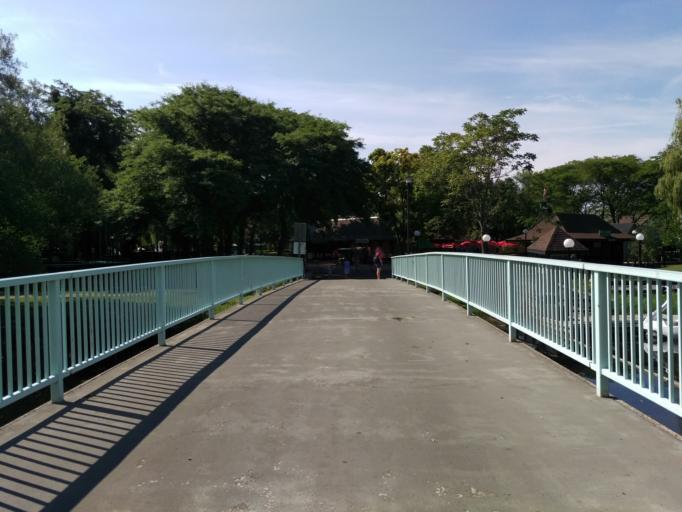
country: CA
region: Ontario
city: Toronto
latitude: 43.6214
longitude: -79.3732
